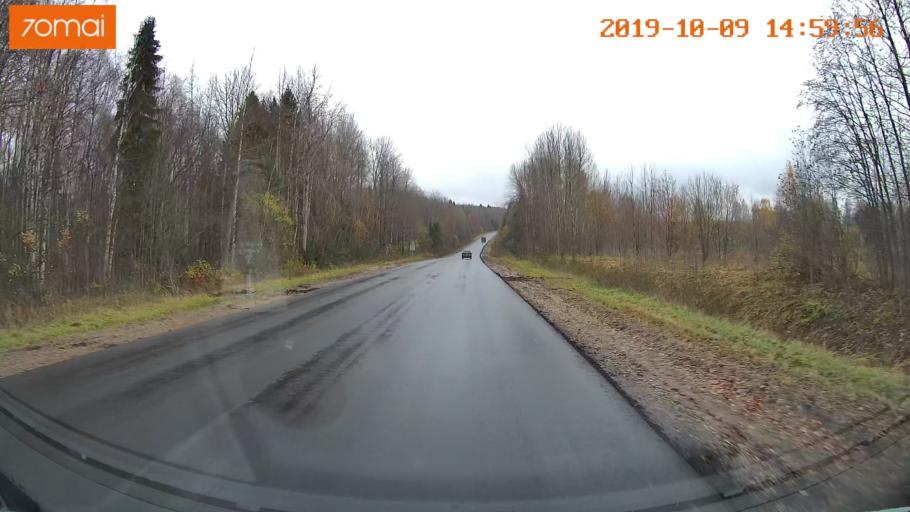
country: RU
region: Kostroma
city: Chistyye Bory
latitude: 58.3147
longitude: 41.6739
